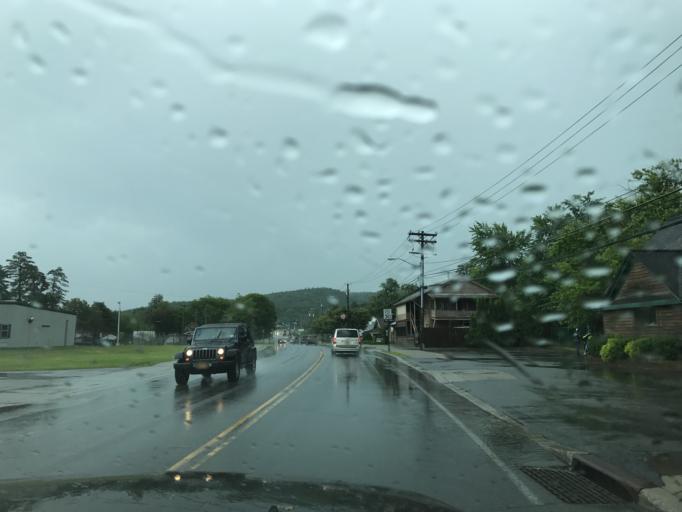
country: US
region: New York
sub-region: Warren County
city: Warrensburg
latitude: 43.4893
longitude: -73.7645
